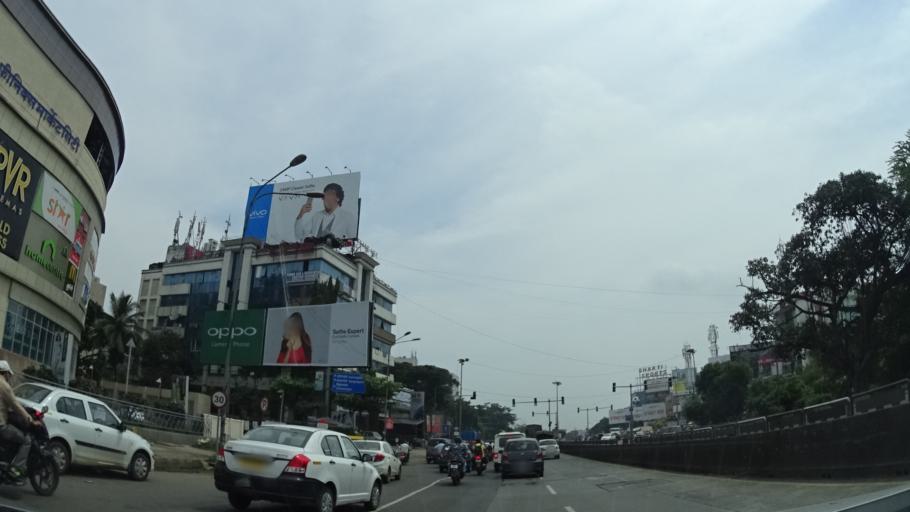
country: IN
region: Maharashtra
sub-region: Pune Division
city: Lohogaon
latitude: 18.5607
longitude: 73.9173
